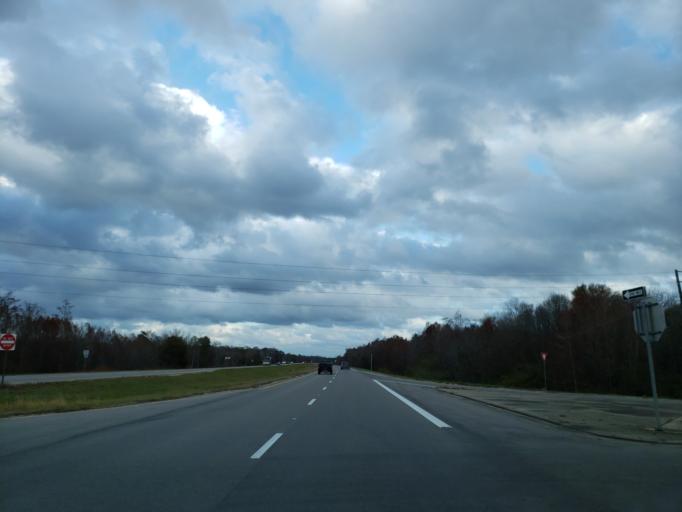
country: US
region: Mississippi
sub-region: Perry County
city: New Augusta
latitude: 31.1198
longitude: -88.8377
